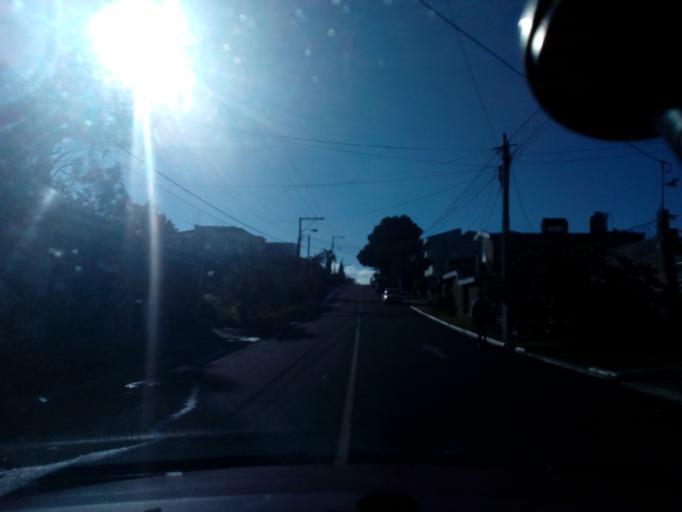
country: GT
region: Guatemala
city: Mixco
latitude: 14.6044
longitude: -90.5795
